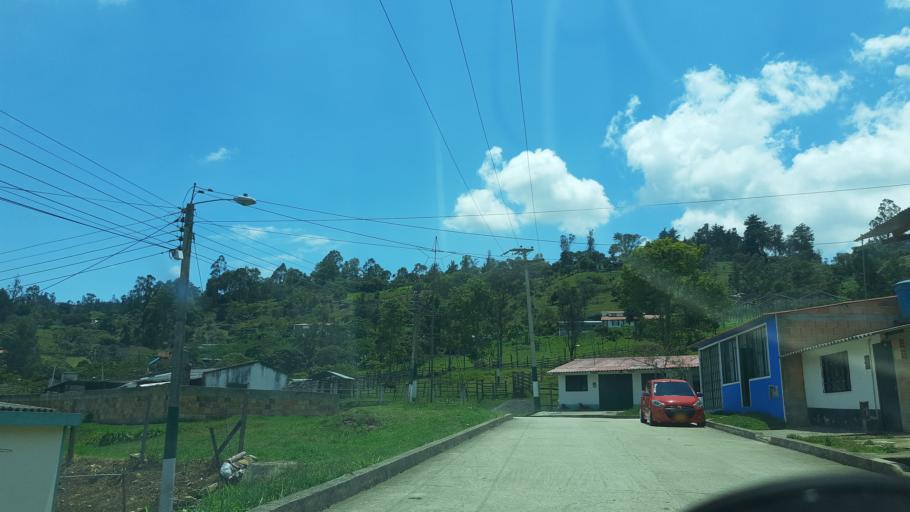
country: CO
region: Boyaca
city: Chinavita
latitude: 5.1421
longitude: -73.3991
